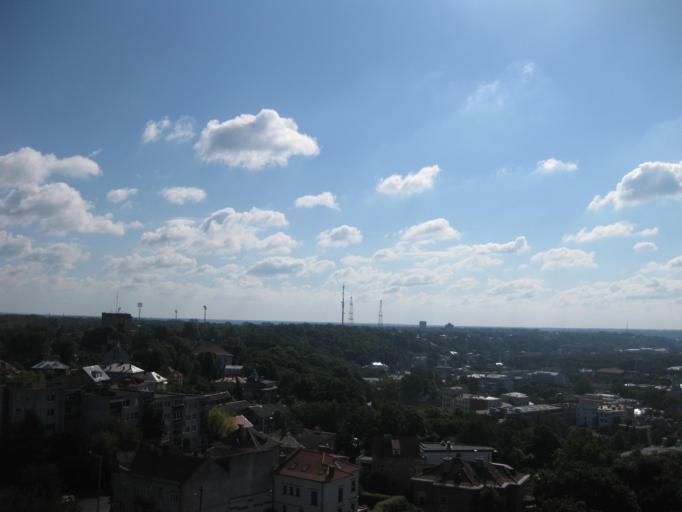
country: LT
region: Kauno apskritis
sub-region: Kaunas
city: Kaunas
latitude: 54.9027
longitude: 23.9171
